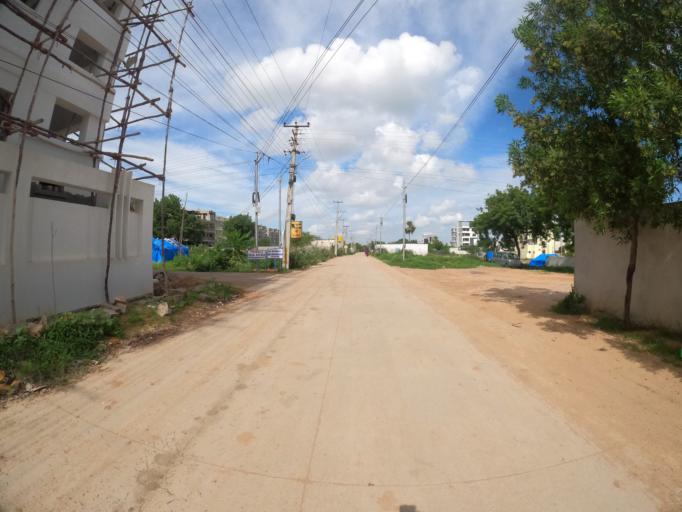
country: IN
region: Telangana
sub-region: Hyderabad
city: Hyderabad
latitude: 17.3517
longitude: 78.3949
